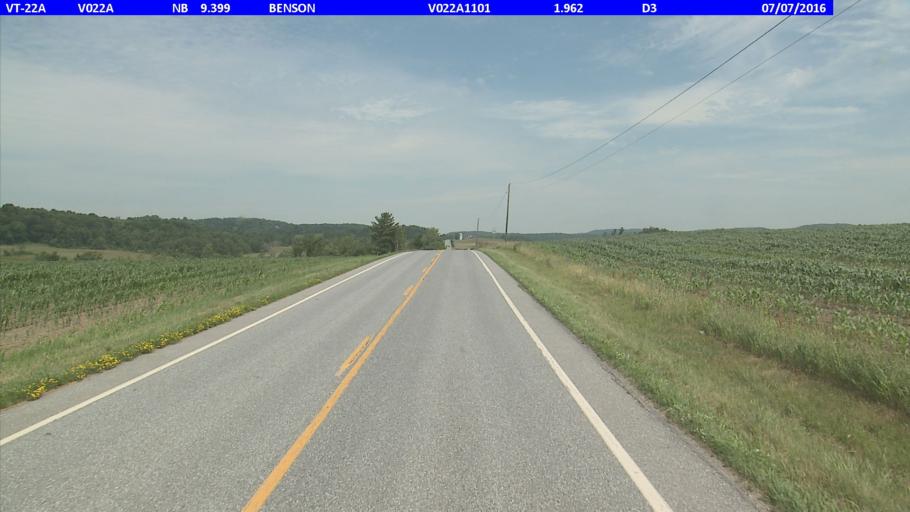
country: US
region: Vermont
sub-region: Rutland County
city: Fair Haven
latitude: 43.6968
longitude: -73.2941
